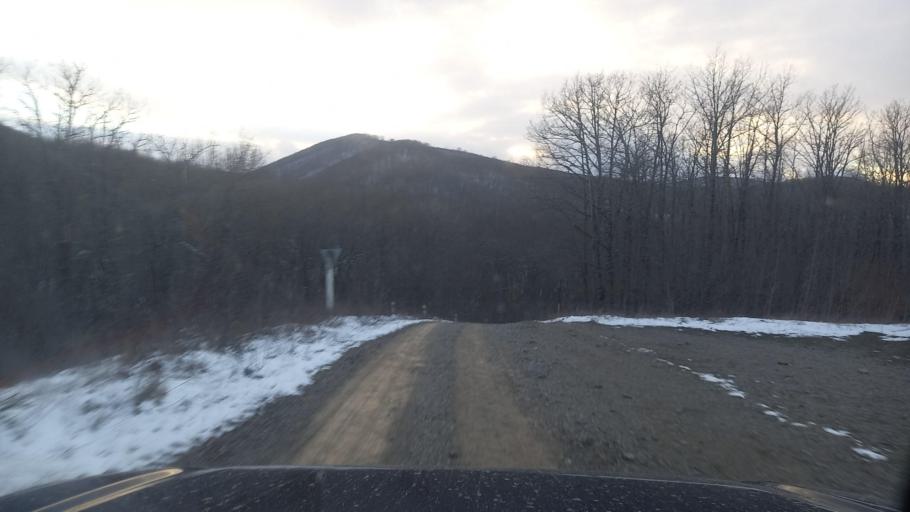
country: RU
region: Krasnodarskiy
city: Smolenskaya
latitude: 44.6794
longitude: 38.7875
